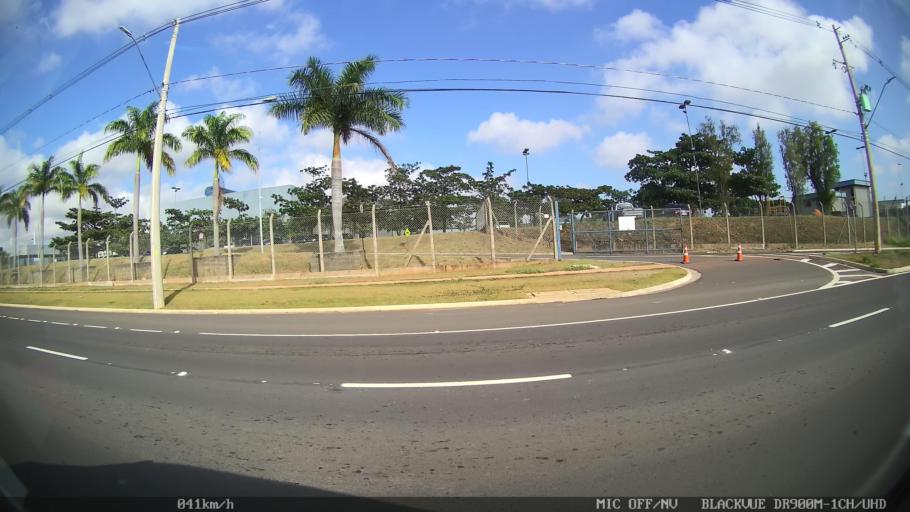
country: BR
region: Sao Paulo
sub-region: Hortolandia
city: Hortolandia
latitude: -22.9036
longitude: -47.1853
